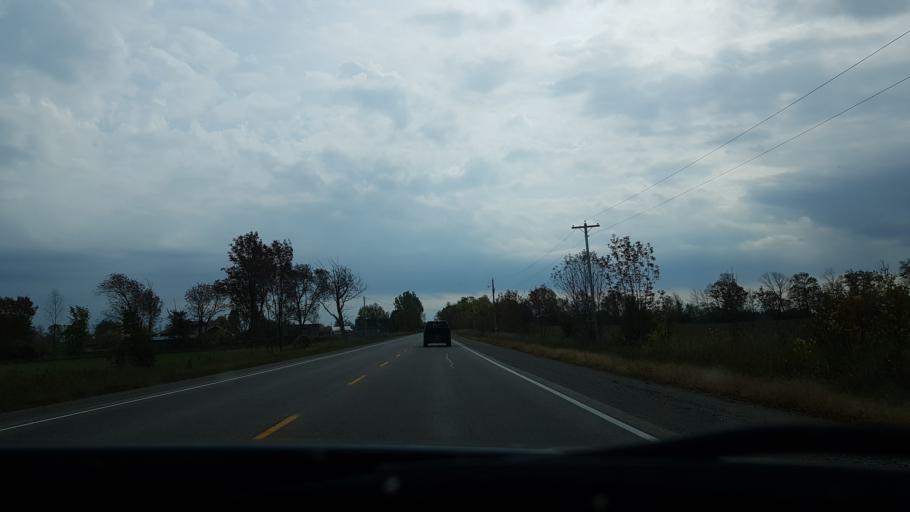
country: CA
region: Ontario
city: Omemee
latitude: 44.4718
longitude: -78.7611
